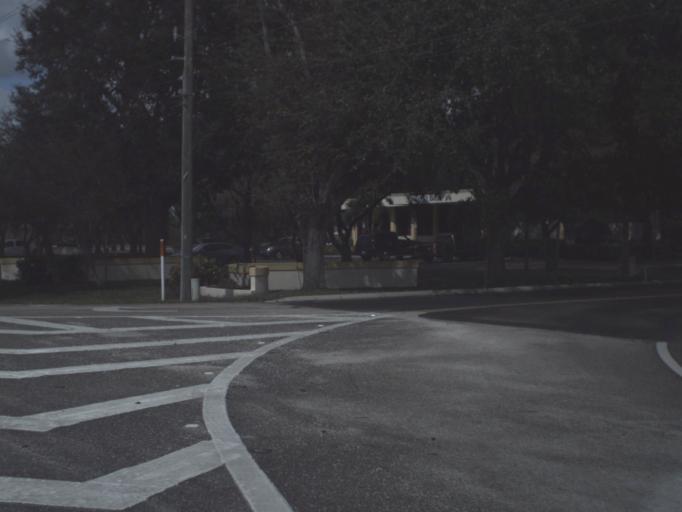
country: US
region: Florida
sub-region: Lee County
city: Olga
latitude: 26.7102
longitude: -81.7194
